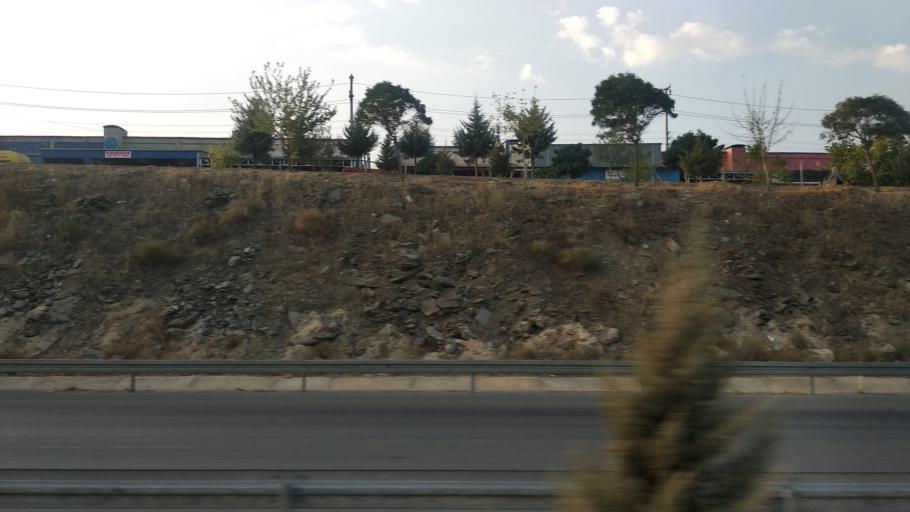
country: TR
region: Manisa
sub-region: Kula
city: Kula
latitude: 38.5471
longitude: 28.6697
